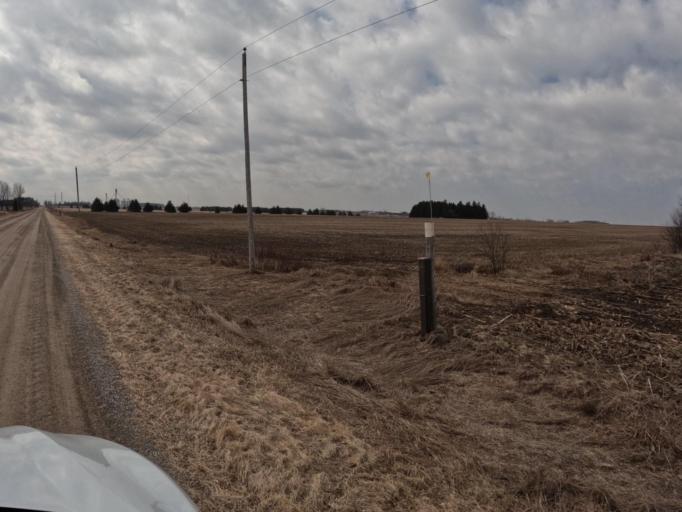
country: CA
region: Ontario
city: Orangeville
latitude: 43.9290
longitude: -80.2413
